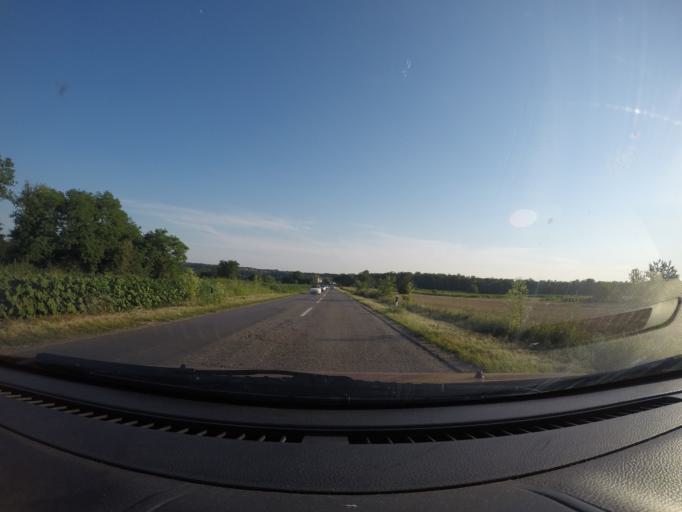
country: RS
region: Central Serbia
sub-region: Branicevski Okrug
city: Malo Crnice
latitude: 44.6851
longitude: 21.3448
